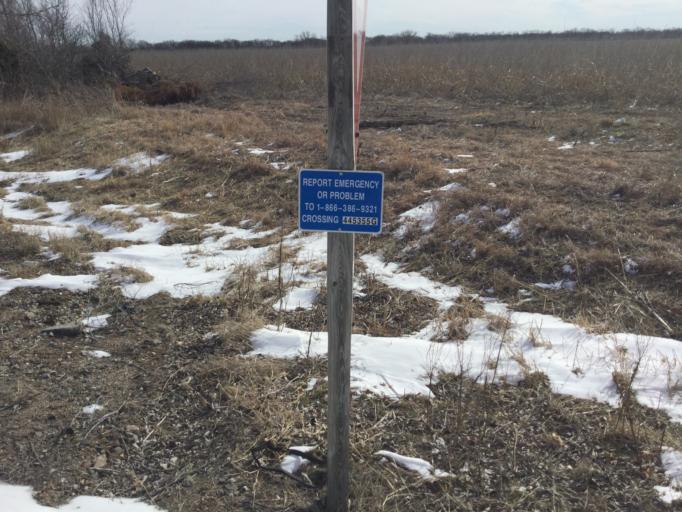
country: US
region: Kansas
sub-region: Sedgwick County
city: Clearwater
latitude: 37.5565
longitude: -97.4432
